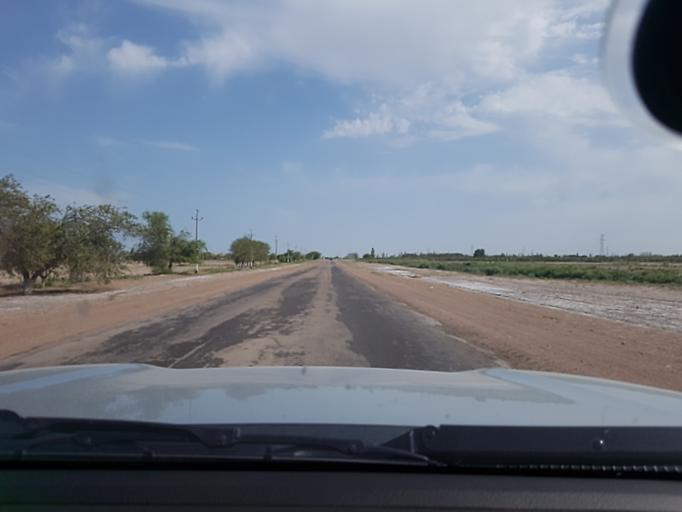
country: TM
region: Dasoguz
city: Boldumsaz
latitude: 42.1065
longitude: 59.7010
